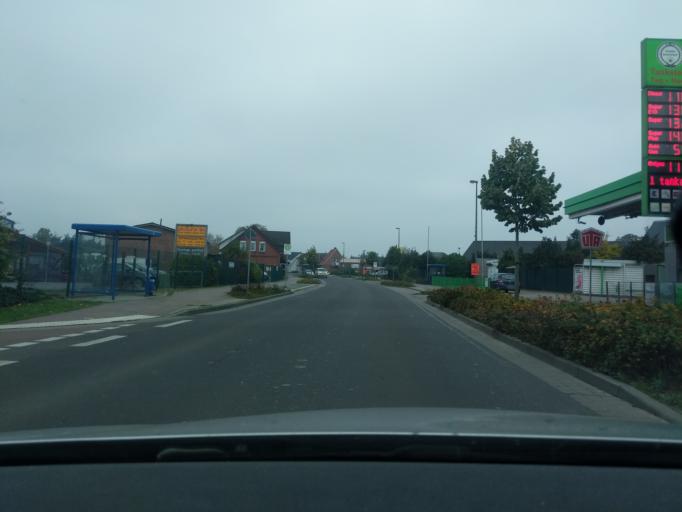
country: DE
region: Lower Saxony
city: Hemmoor
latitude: 53.6810
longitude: 9.1793
